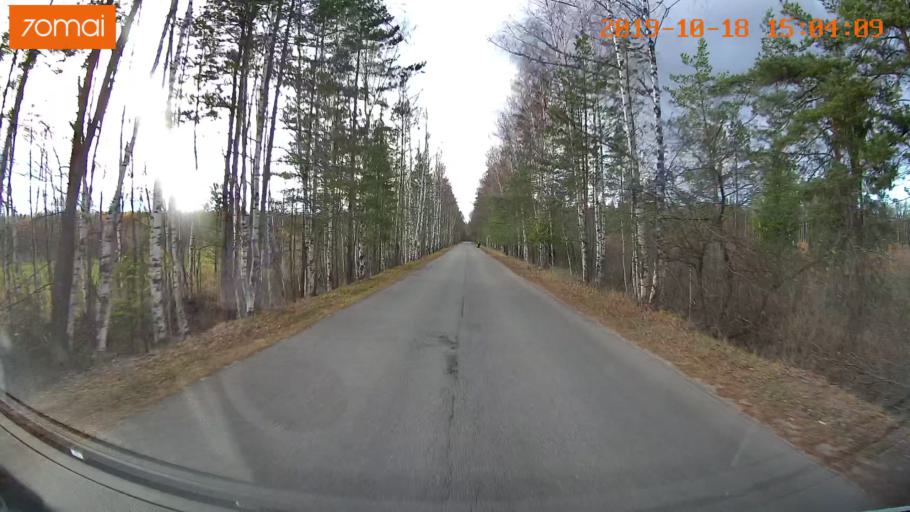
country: RU
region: Vladimir
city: Kurlovo
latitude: 55.5041
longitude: 40.5794
